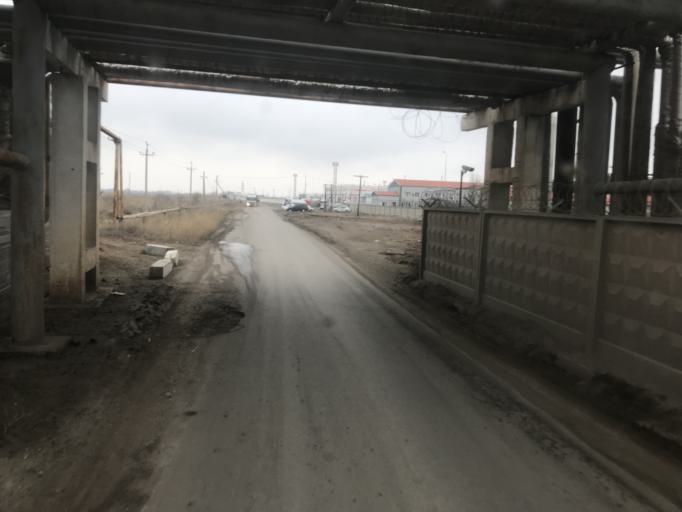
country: RU
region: Volgograd
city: Svetlyy Yar
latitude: 48.5084
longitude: 44.6412
